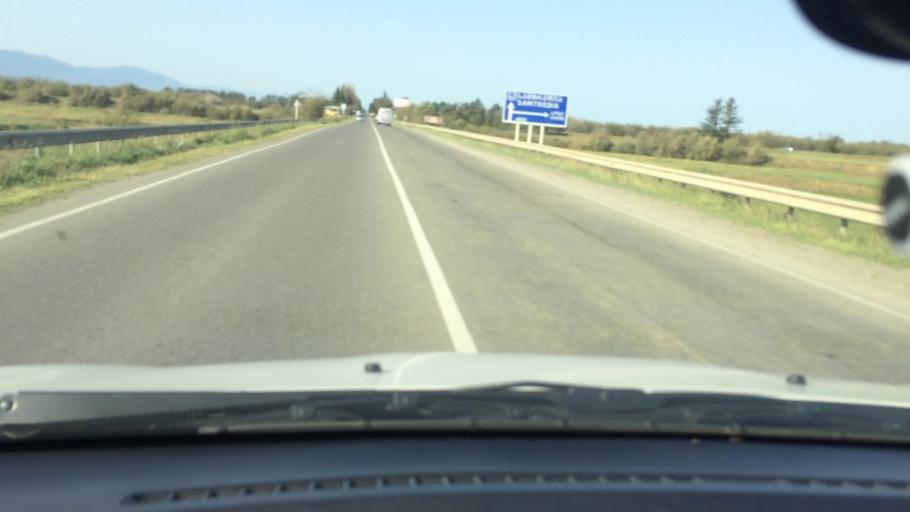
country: GE
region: Imereti
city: K'ulashi
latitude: 42.1731
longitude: 42.4272
